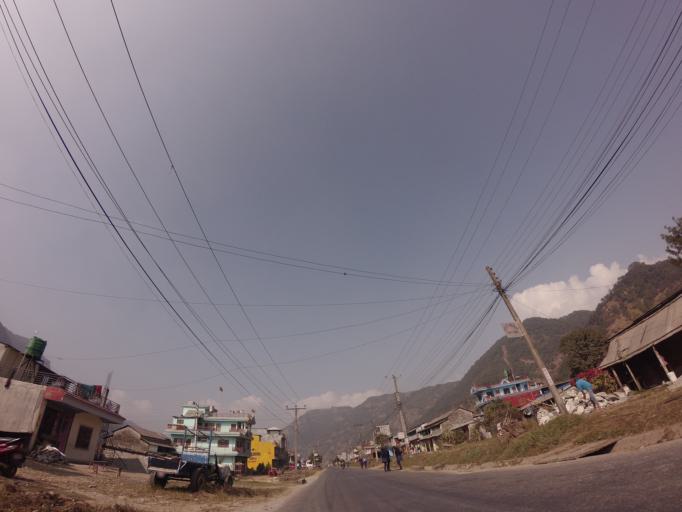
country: NP
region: Western Region
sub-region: Gandaki Zone
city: Pokhara
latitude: 28.2793
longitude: 83.9307
